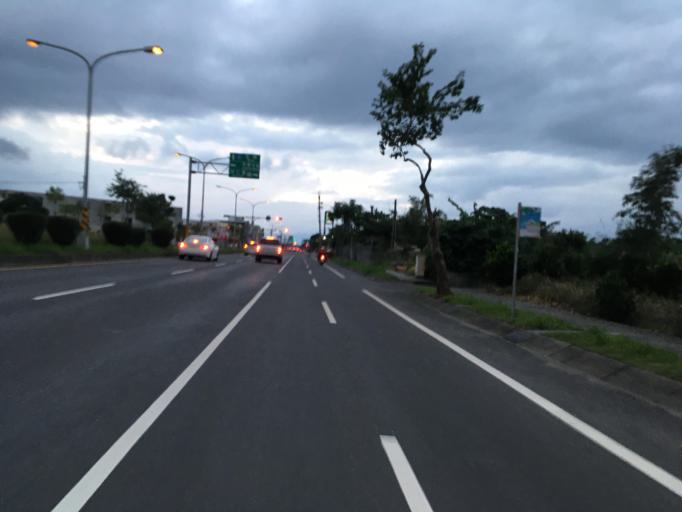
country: TW
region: Taiwan
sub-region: Yilan
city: Yilan
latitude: 24.6228
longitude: 121.8390
